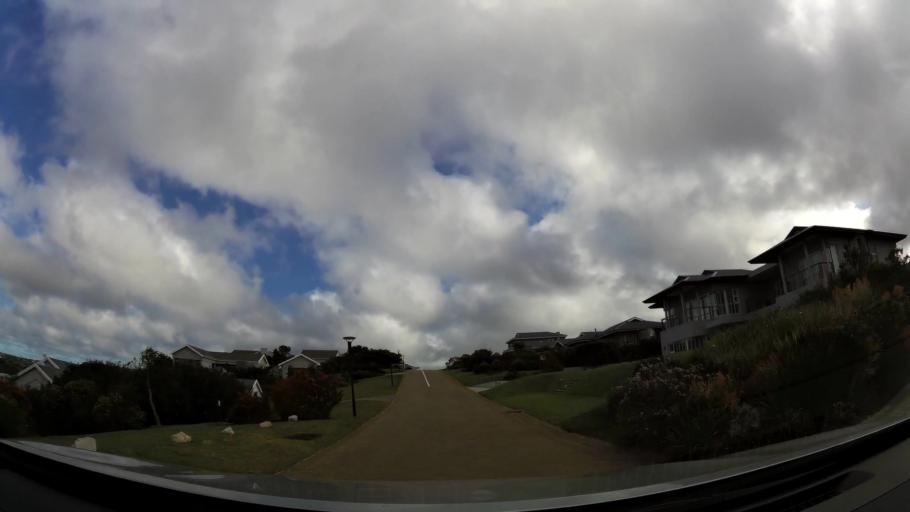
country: ZA
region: Western Cape
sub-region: Eden District Municipality
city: Plettenberg Bay
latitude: -34.0661
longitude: 23.3568
